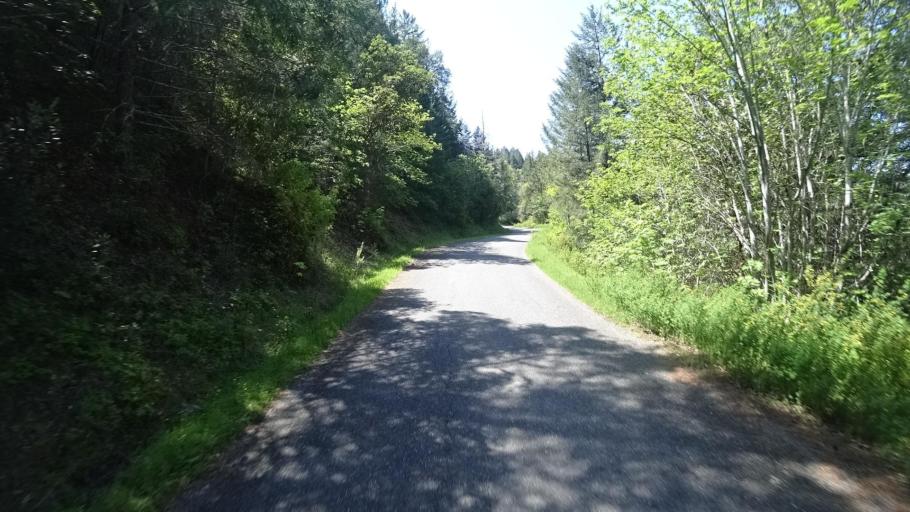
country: US
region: California
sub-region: Humboldt County
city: Redway
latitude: 40.1887
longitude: -123.5750
